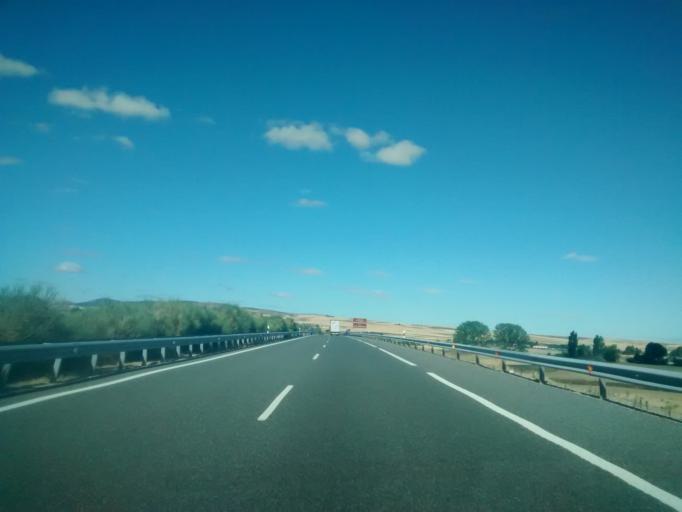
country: ES
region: Castille and Leon
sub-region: Provincia de Avila
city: San Pedro del Arroyo
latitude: 40.8087
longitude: -4.8807
